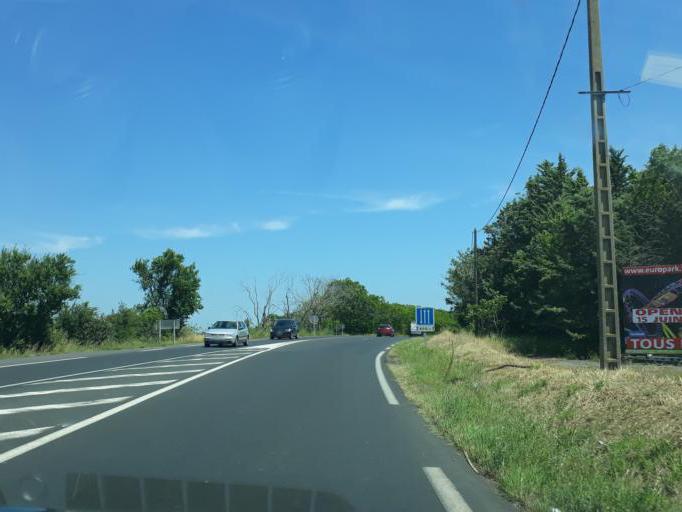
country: FR
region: Languedoc-Roussillon
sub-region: Departement de l'Herault
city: Vias
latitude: 43.3148
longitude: 3.3819
